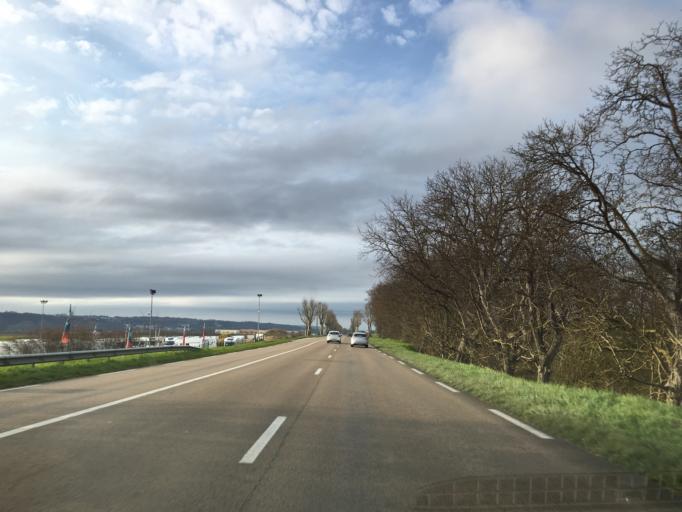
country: FR
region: Bourgogne
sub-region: Departement de l'Yonne
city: Maillot
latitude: 48.1616
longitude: 3.3022
